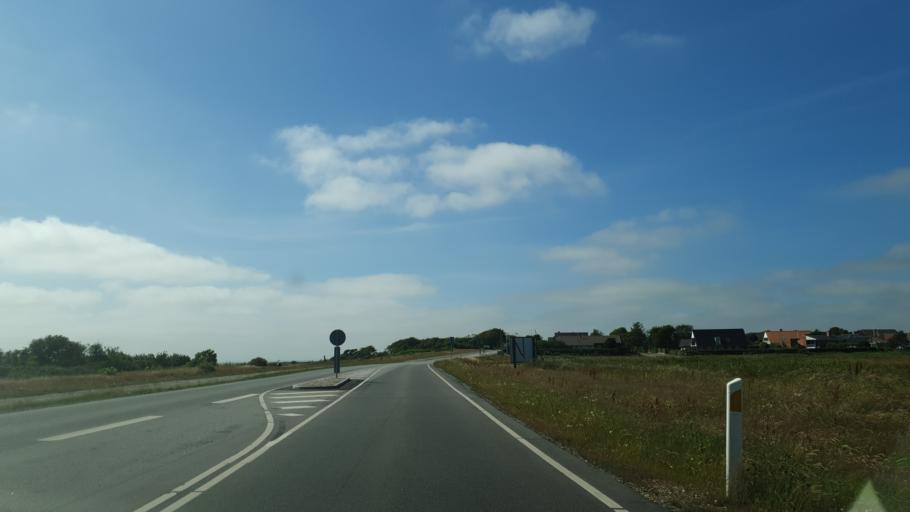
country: DK
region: Central Jutland
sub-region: Ringkobing-Skjern Kommune
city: Ringkobing
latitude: 56.0685
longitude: 8.2806
